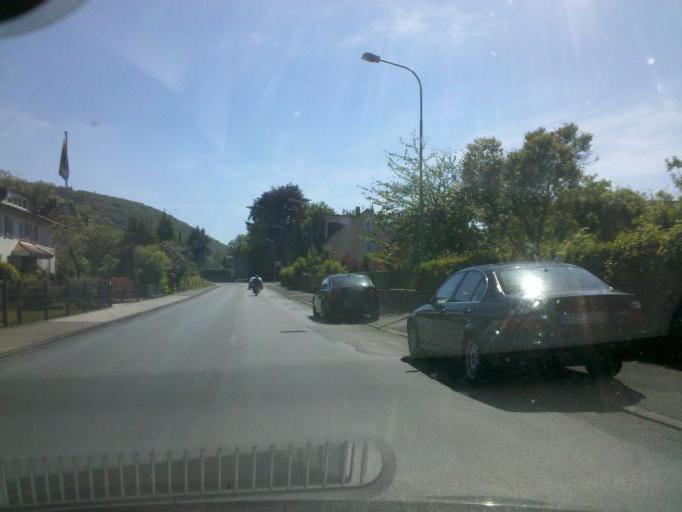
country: DE
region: Hesse
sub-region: Regierungsbezirk Giessen
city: Haiger
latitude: 50.7382
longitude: 8.1995
